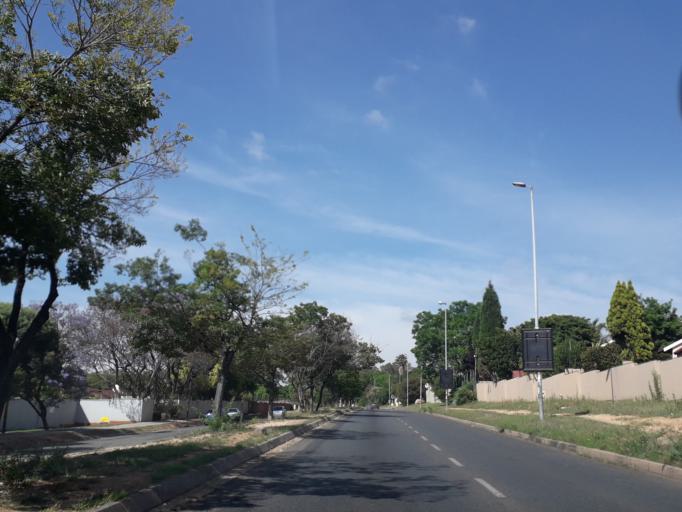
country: ZA
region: Gauteng
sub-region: City of Johannesburg Metropolitan Municipality
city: Roodepoort
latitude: -26.0745
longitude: 27.9617
